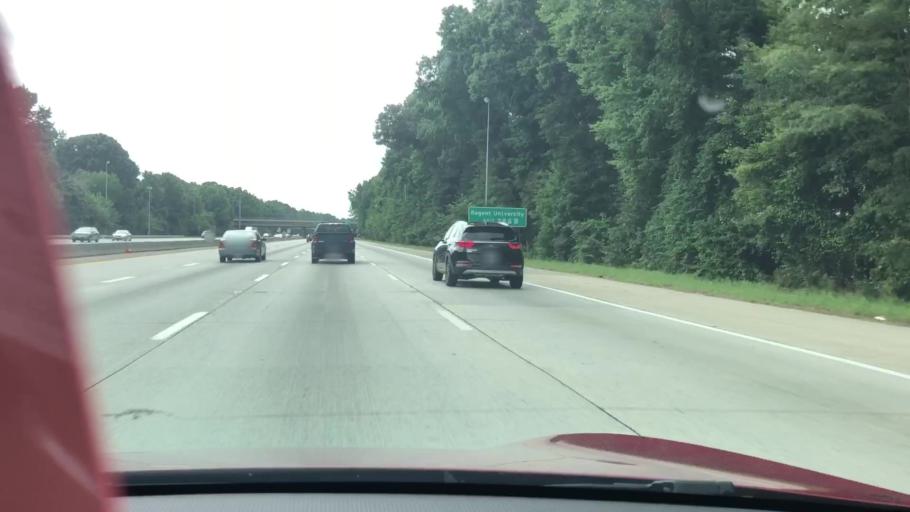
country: US
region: Virginia
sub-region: City of Chesapeake
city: Chesapeake
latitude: 36.8170
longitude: -76.1950
